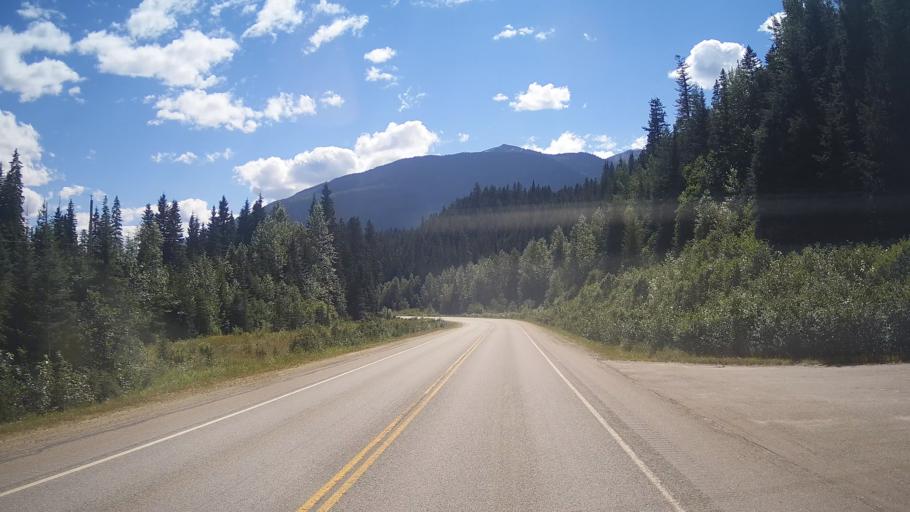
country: CA
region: Alberta
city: Jasper Park Lodge
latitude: 52.5658
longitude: -119.1053
